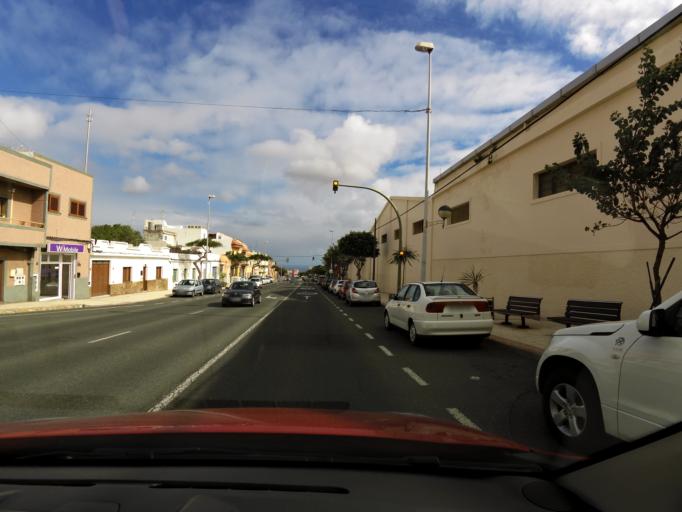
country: ES
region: Canary Islands
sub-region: Provincia de Las Palmas
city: Ingenio
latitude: 27.9182
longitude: -15.4326
